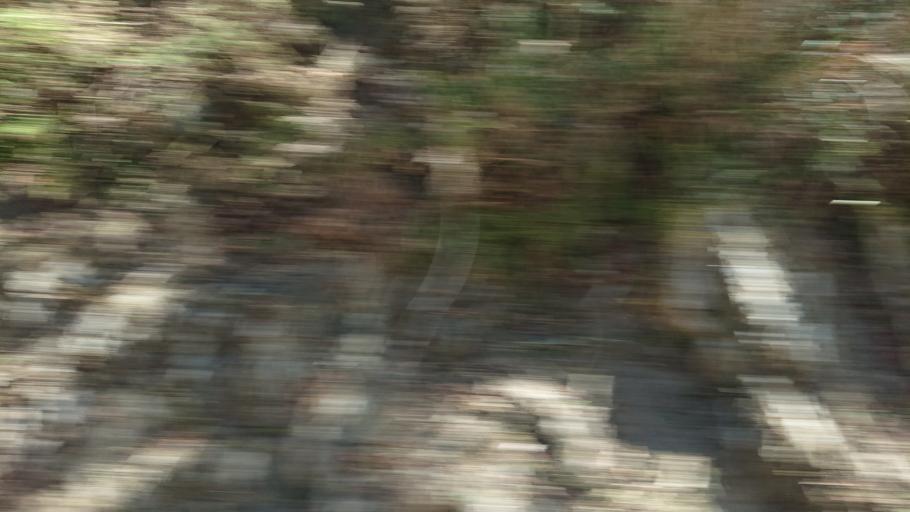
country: TW
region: Taiwan
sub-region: Hualien
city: Hualian
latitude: 24.3732
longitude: 121.3397
